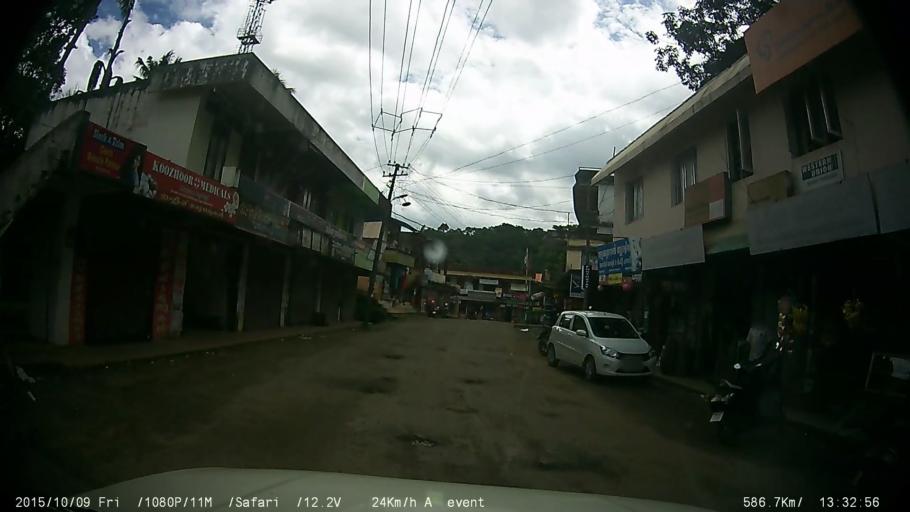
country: IN
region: Kerala
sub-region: Ernakulam
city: Ramamangalam
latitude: 9.9091
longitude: 76.5582
